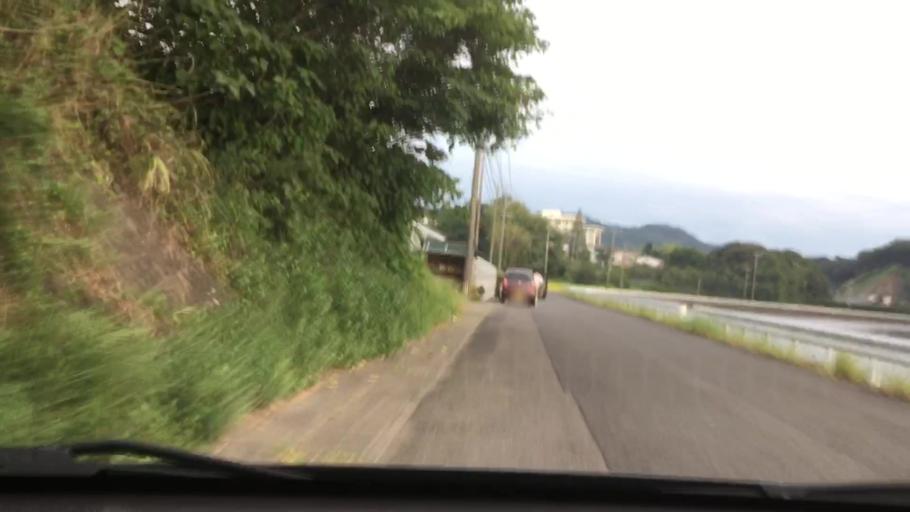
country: JP
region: Nagasaki
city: Sasebo
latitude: 32.9915
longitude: 129.7718
